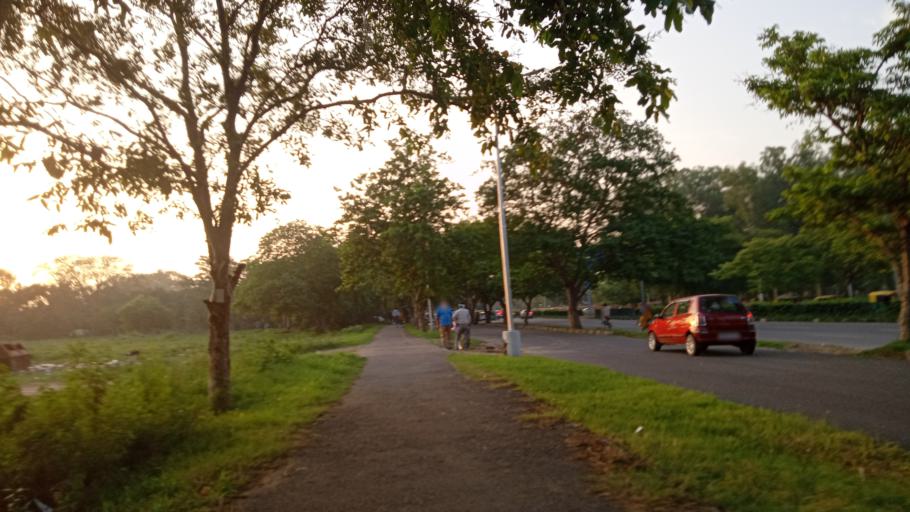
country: IN
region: Chandigarh
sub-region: Chandigarh
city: Chandigarh
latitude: 30.7495
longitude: 76.7501
